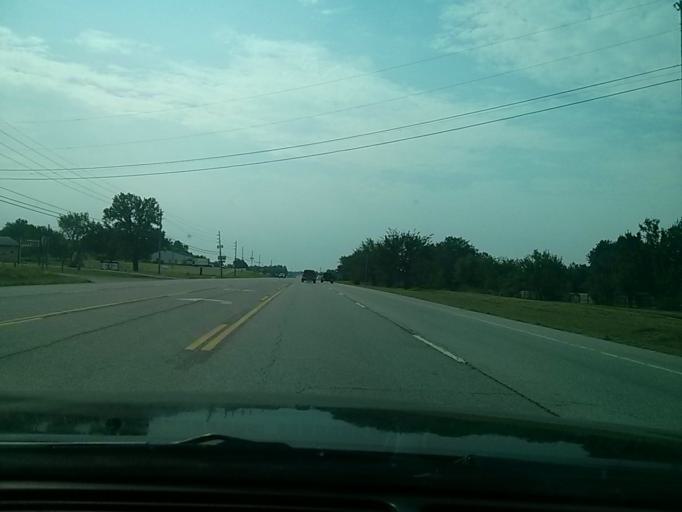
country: US
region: Oklahoma
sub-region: Wagoner County
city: Coweta
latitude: 35.9788
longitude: -95.6650
